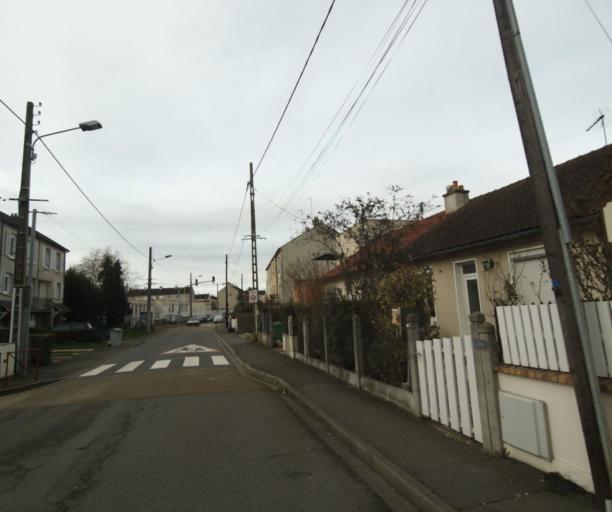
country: FR
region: Pays de la Loire
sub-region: Departement de la Sarthe
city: Coulaines
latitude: 48.0094
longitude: 0.2228
